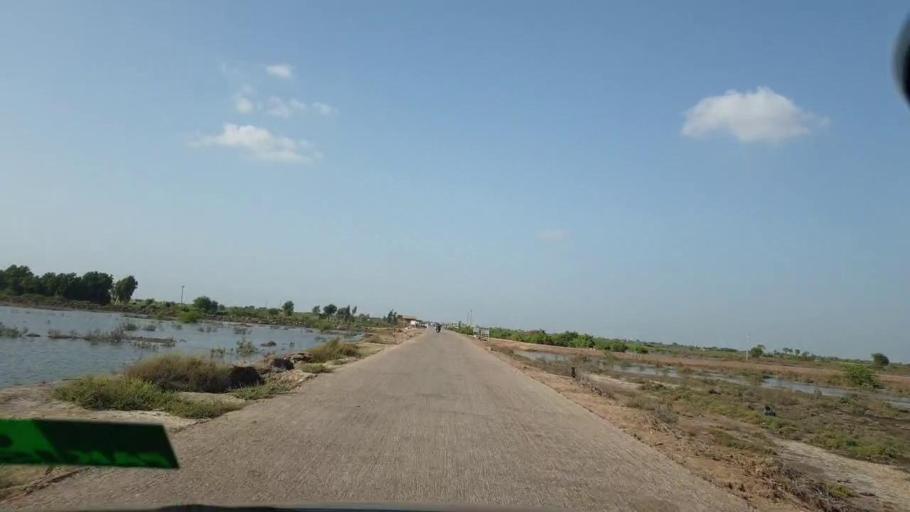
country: PK
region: Sindh
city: Naukot
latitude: 24.7395
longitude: 69.1983
